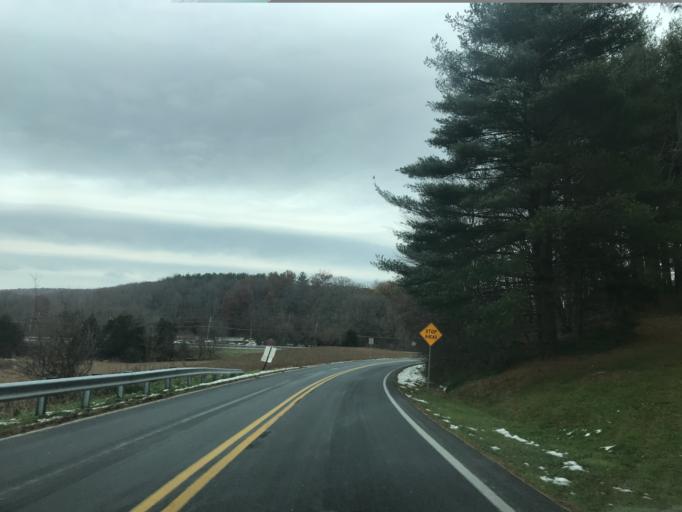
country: US
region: Pennsylvania
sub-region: York County
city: Susquehanna Trails
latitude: 39.6897
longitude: -76.3761
